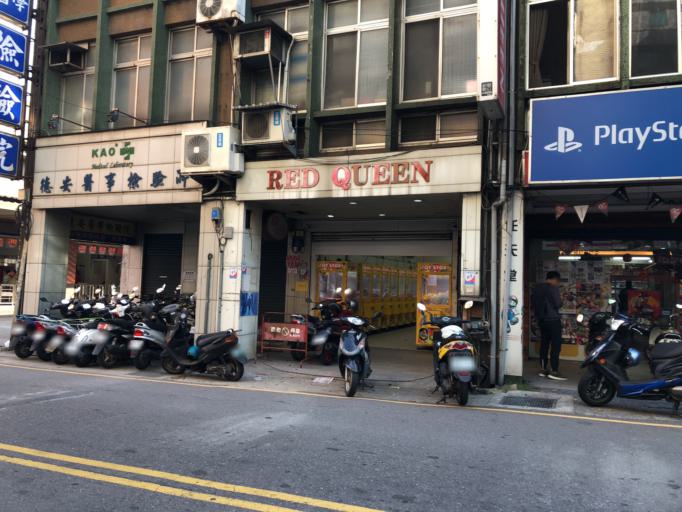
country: TW
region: Taiwan
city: Taoyuan City
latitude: 24.9534
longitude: 121.2237
